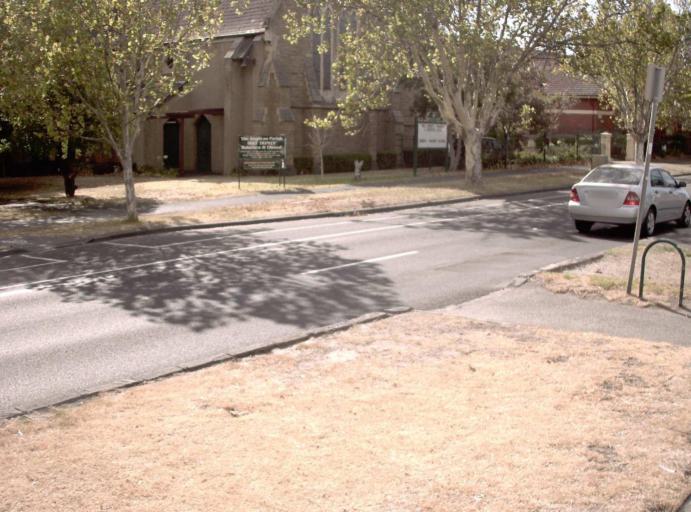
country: AU
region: Victoria
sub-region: Port Phillip
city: Saint Kilda
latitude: -37.8706
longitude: 144.9888
